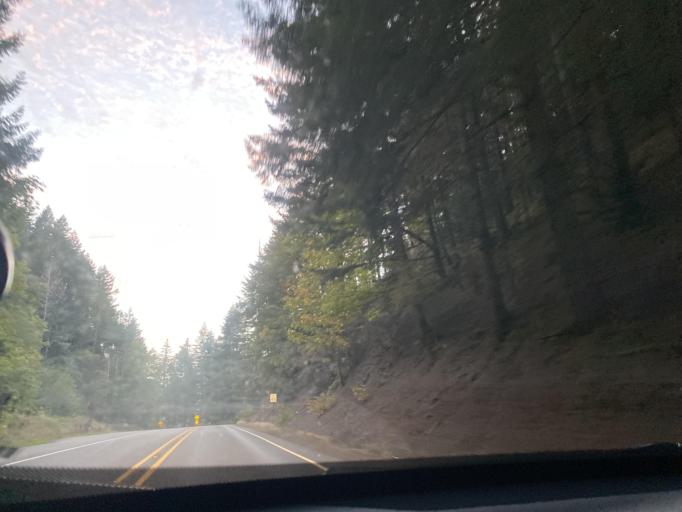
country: CA
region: British Columbia
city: Sooke
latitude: 48.0810
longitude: -123.7372
